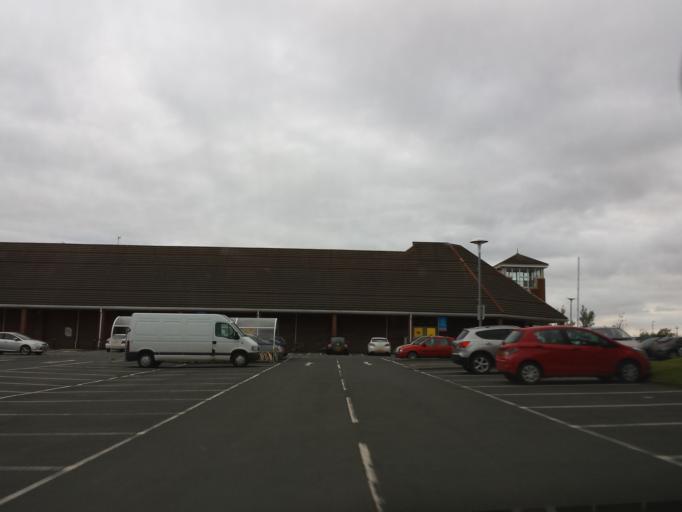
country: GB
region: Scotland
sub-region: South Ayrshire
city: Prestwick
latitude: 55.4678
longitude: -4.6063
